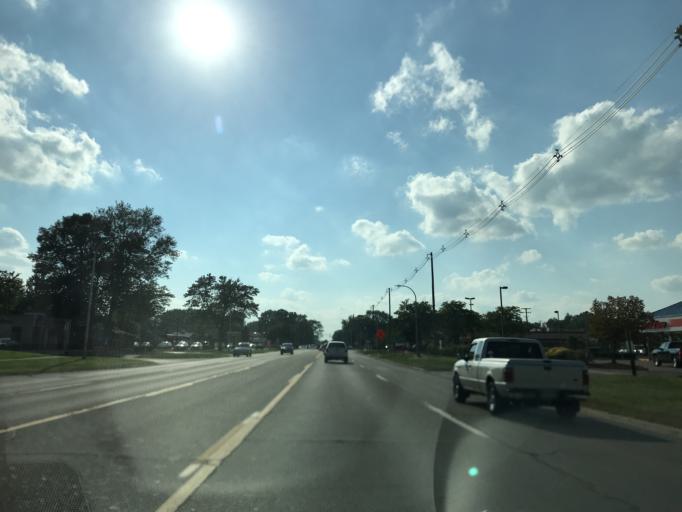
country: US
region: Michigan
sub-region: Wayne County
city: Livonia
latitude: 42.3978
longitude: -83.3506
